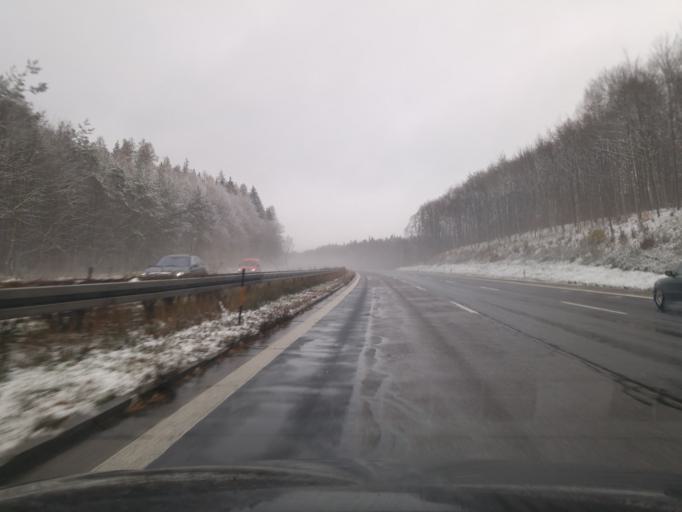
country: DE
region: Bavaria
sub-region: Regierungsbezirk Unterfranken
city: Elfershausen
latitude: 50.1697
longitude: 9.9633
